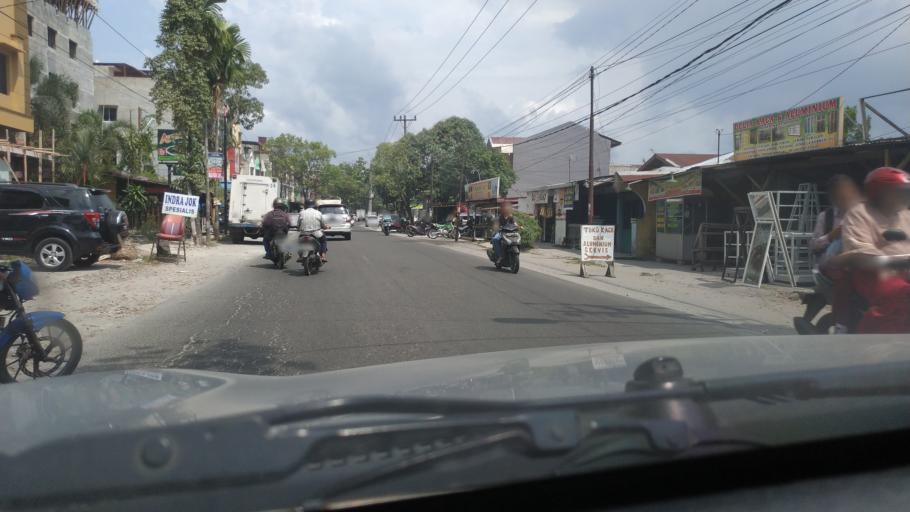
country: ID
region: North Sumatra
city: Sunggal
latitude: 3.5855
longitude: 98.6203
